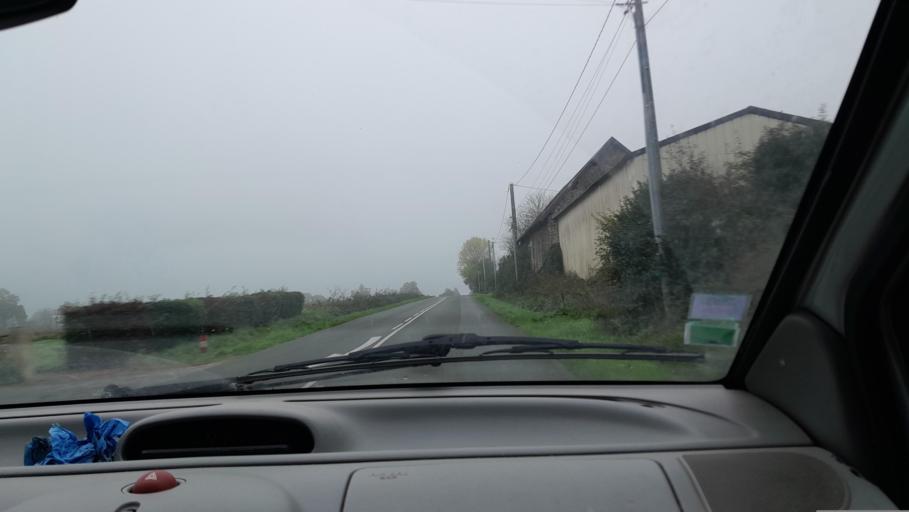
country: FR
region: Pays de la Loire
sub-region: Departement de la Mayenne
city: Ahuille
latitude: 48.0423
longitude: -0.8842
